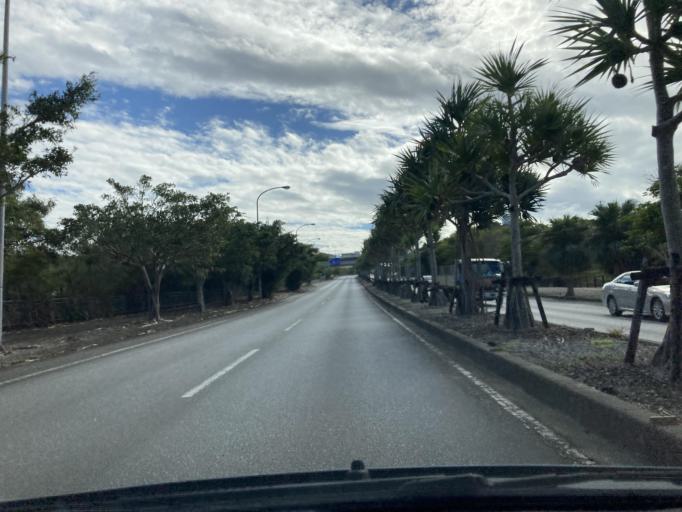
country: JP
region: Okinawa
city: Tomigusuku
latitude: 26.1677
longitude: 127.7259
